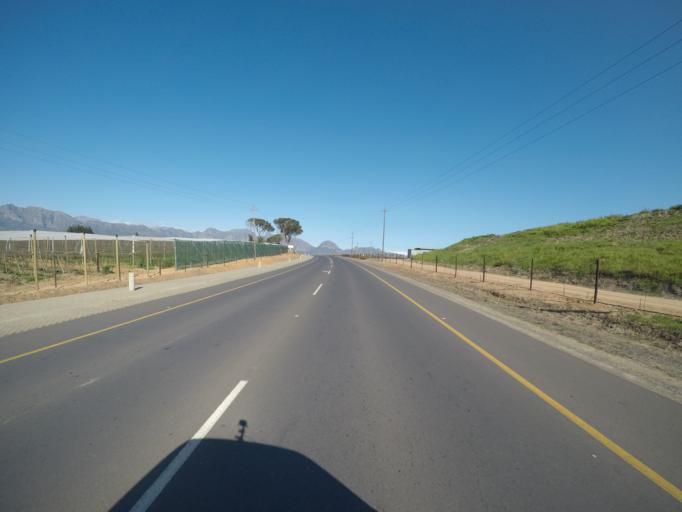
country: ZA
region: Western Cape
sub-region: Cape Winelands District Municipality
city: Noorder-Paarl
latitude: -33.6882
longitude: 18.9499
